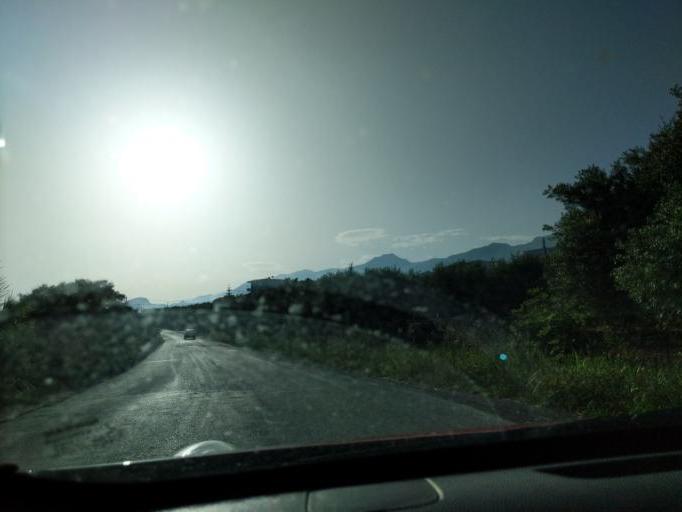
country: GR
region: Crete
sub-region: Nomos Rethymnis
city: Atsipopoulon
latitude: 35.1817
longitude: 24.4194
